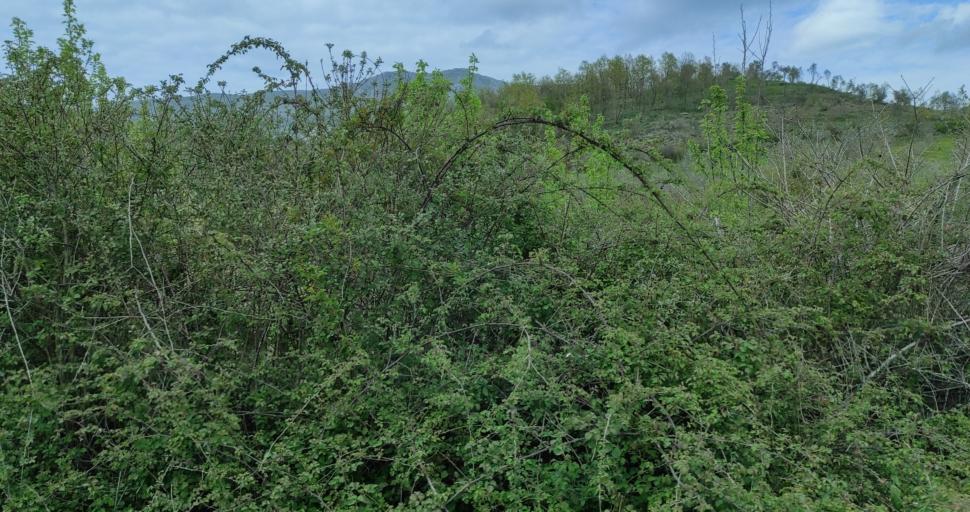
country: AL
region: Shkoder
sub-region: Rrethi i Shkodres
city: Dajc
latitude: 42.0351
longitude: 19.4043
